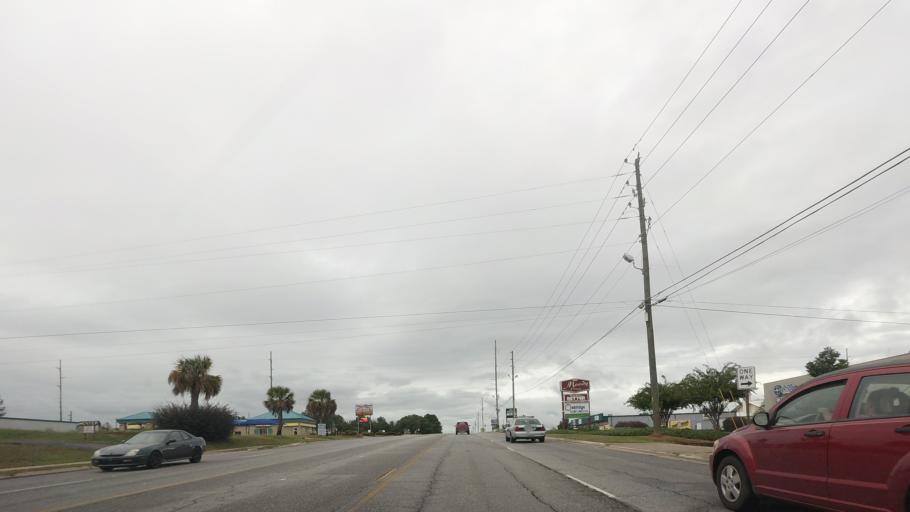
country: US
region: Georgia
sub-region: Houston County
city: Warner Robins
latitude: 32.5879
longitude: -83.6228
